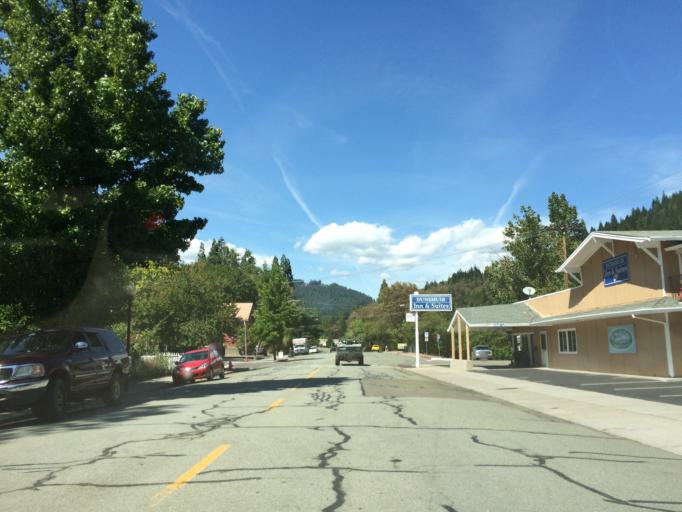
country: US
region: California
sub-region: Siskiyou County
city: Dunsmuir
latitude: 41.2150
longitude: -122.2725
